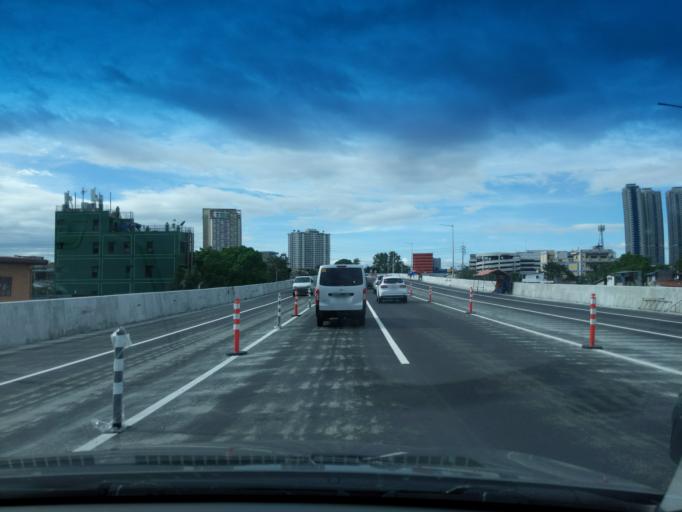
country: PH
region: Metro Manila
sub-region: San Juan
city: San Juan
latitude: 14.6003
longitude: 121.0223
